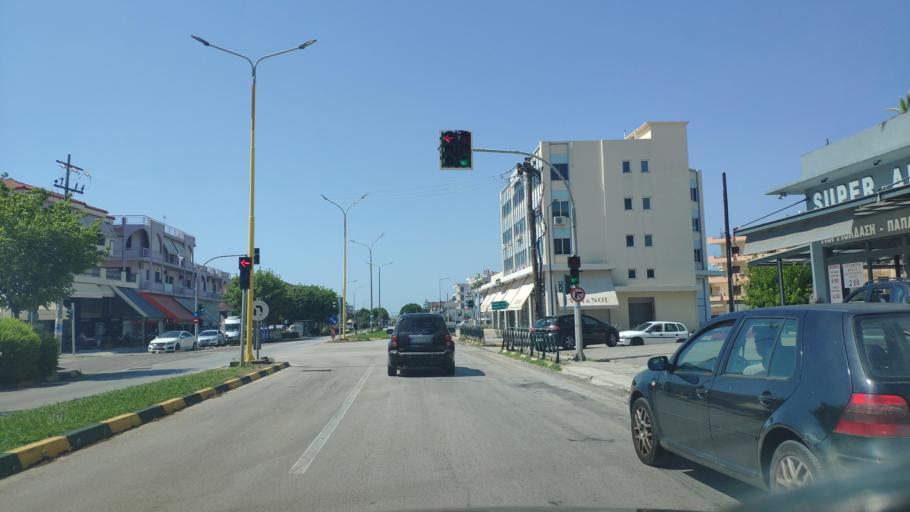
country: GR
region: Epirus
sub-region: Nomos Artas
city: Arta
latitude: 39.1615
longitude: 20.9808
